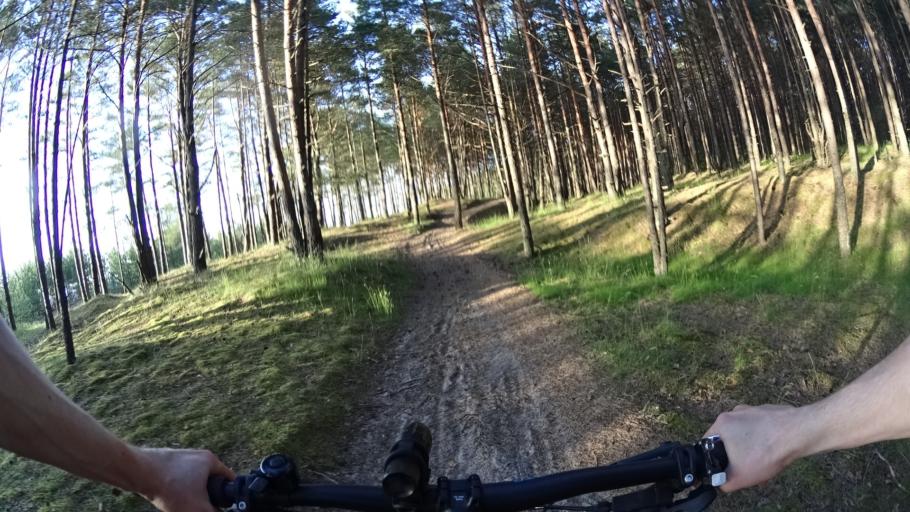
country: LV
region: Riga
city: Jaunciems
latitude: 57.1104
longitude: 24.1844
